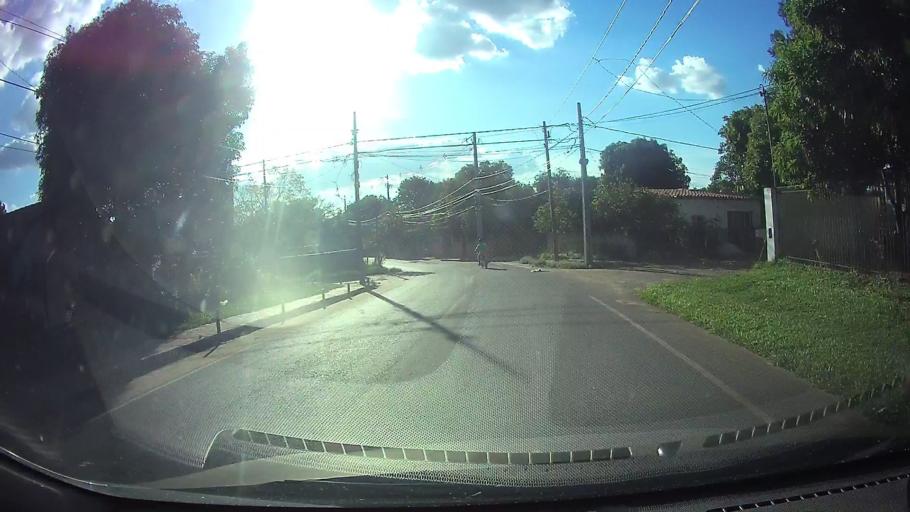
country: PY
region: Central
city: San Lorenzo
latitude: -25.2862
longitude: -57.5021
